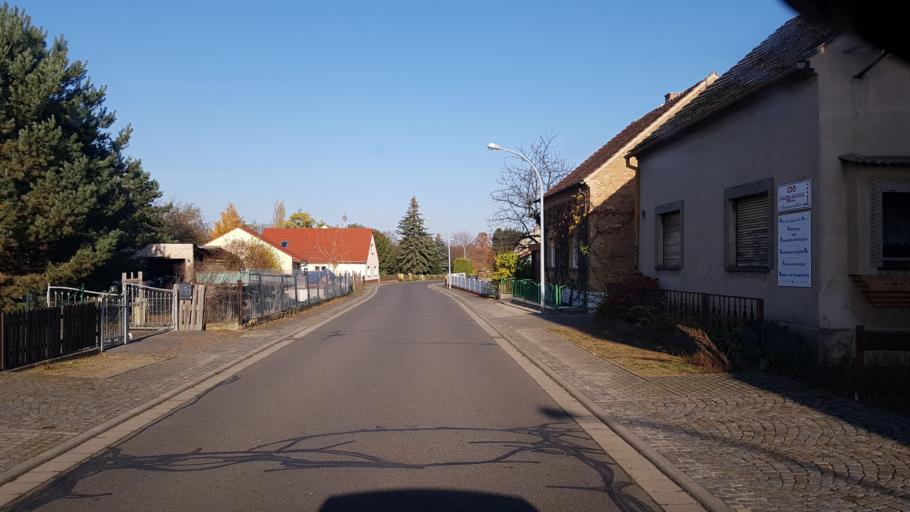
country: DE
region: Brandenburg
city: Schipkau
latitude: 51.5668
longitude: 13.9231
